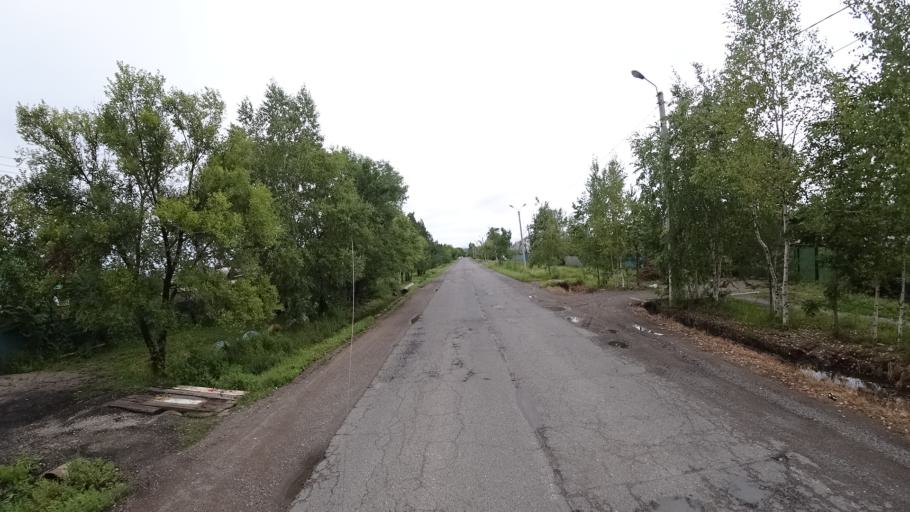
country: RU
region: Primorskiy
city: Monastyrishche
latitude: 44.1999
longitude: 132.4591
